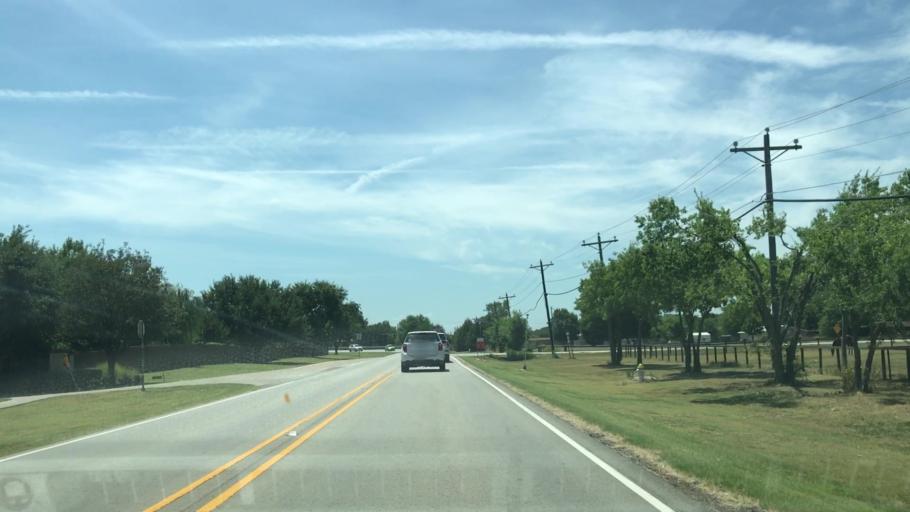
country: US
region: Texas
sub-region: Collin County
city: Lucas
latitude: 33.0776
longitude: -96.5769
